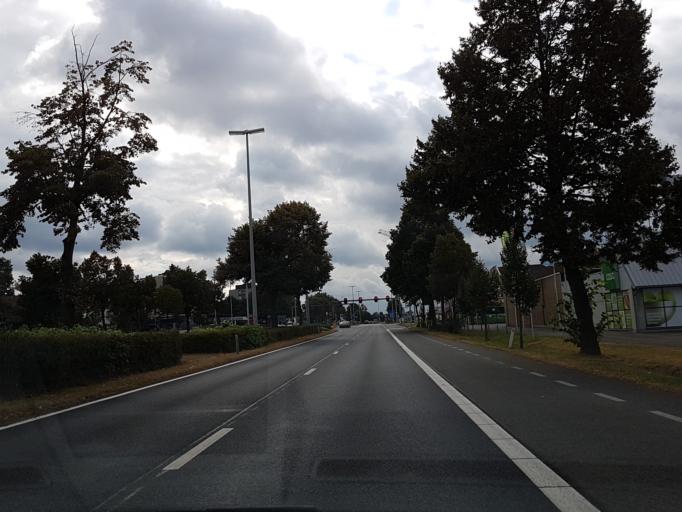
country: BE
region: Flanders
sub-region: Provincie Limburg
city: Sint-Truiden
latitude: 50.8139
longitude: 5.1950
